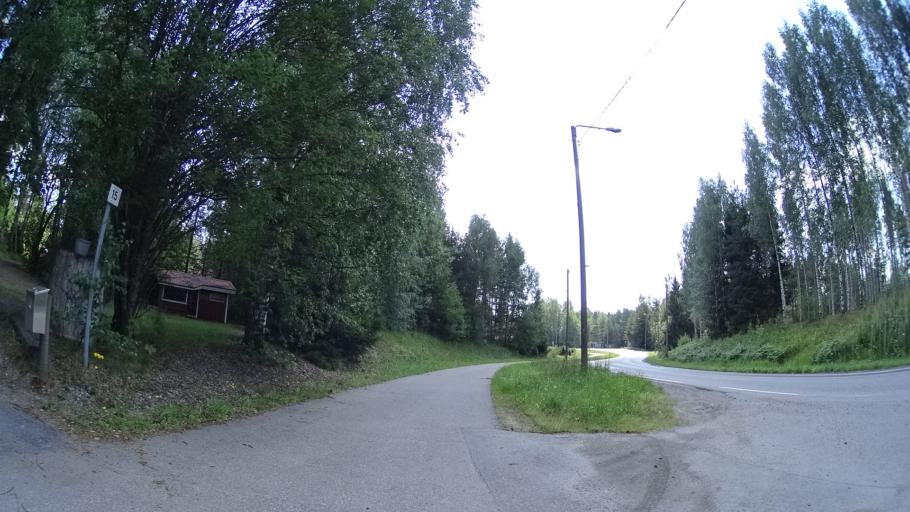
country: FI
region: Uusimaa
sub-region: Helsinki
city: Tuusula
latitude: 60.3489
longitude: 25.0032
